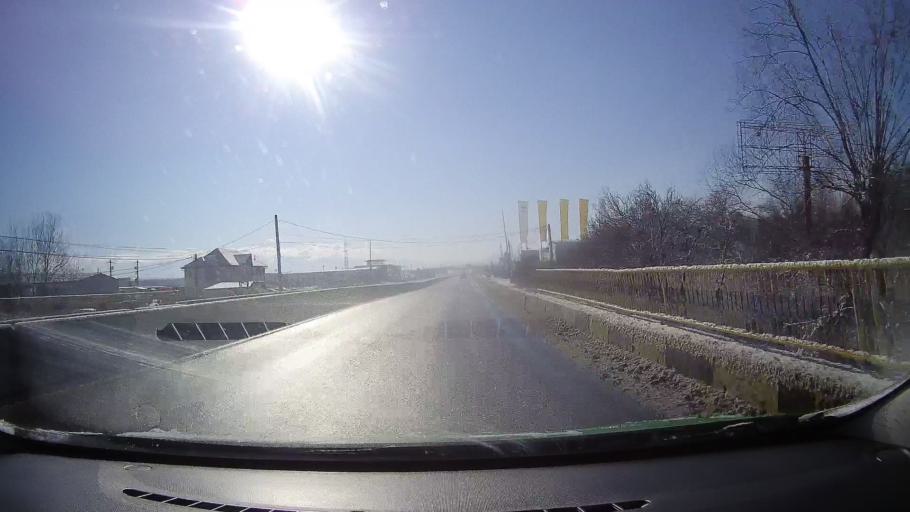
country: RO
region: Sibiu
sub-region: Comuna Selimbar
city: Selimbar
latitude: 45.7554
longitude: 24.1992
